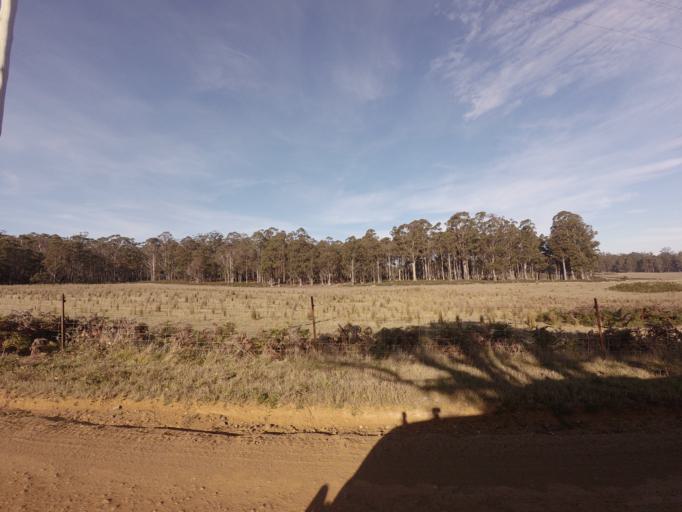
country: AU
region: Tasmania
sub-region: Brighton
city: Bridgewater
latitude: -42.4602
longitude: 147.3790
